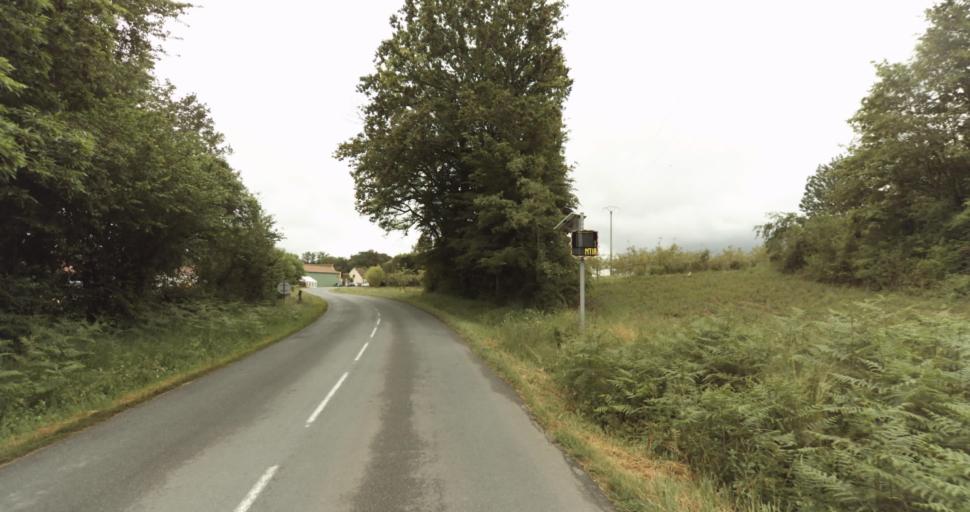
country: FR
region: Aquitaine
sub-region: Departement de la Dordogne
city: Belves
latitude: 44.6964
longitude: 0.9146
